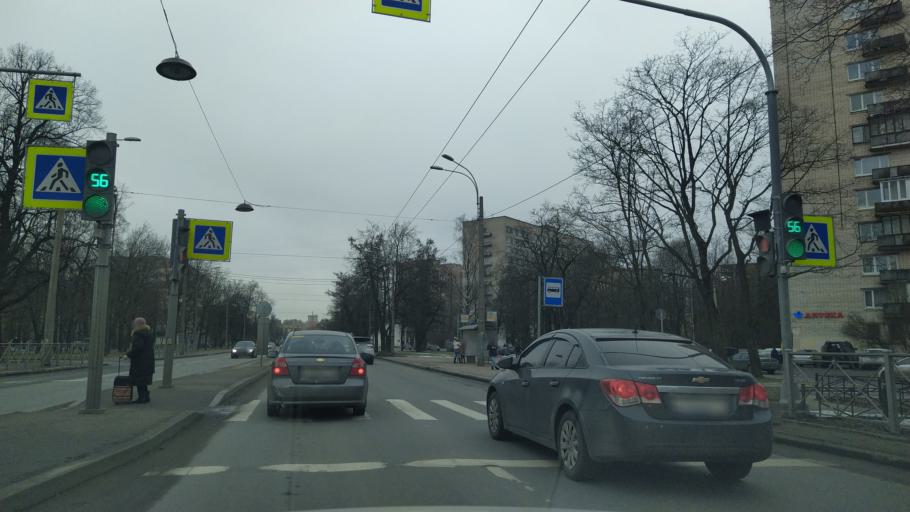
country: RU
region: St.-Petersburg
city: Kushelevka
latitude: 60.0025
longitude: 30.3597
